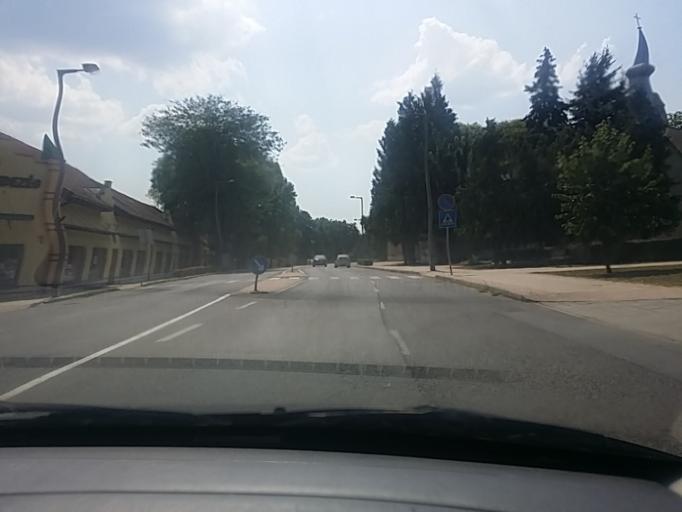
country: HU
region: Tolna
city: Dombovar
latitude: 46.3707
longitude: 18.1297
